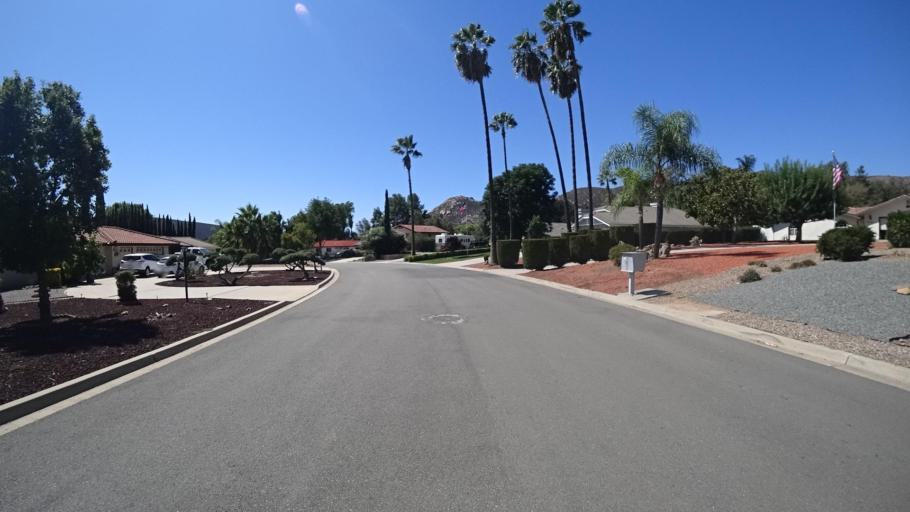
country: US
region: California
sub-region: San Diego County
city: San Diego Country Estates
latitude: 33.0093
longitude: -116.8195
